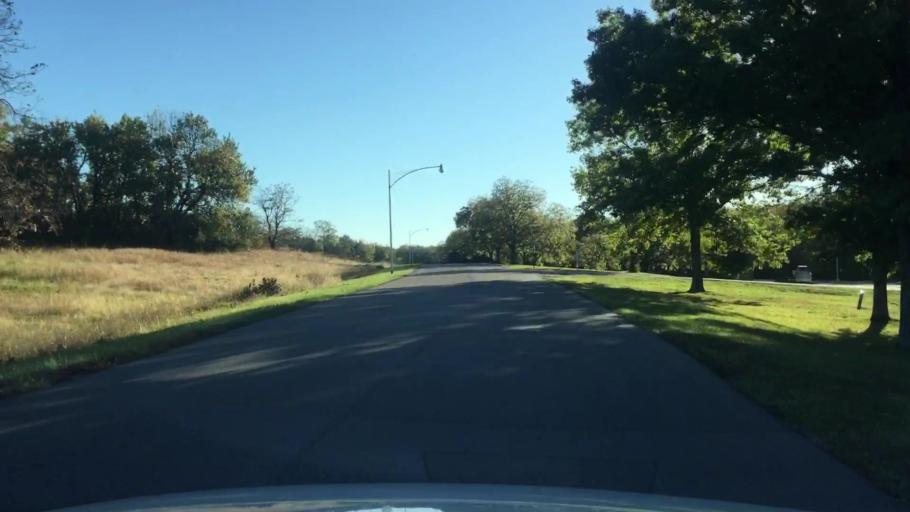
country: US
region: Kansas
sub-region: Johnson County
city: Lenexa
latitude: 38.9826
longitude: -94.7900
